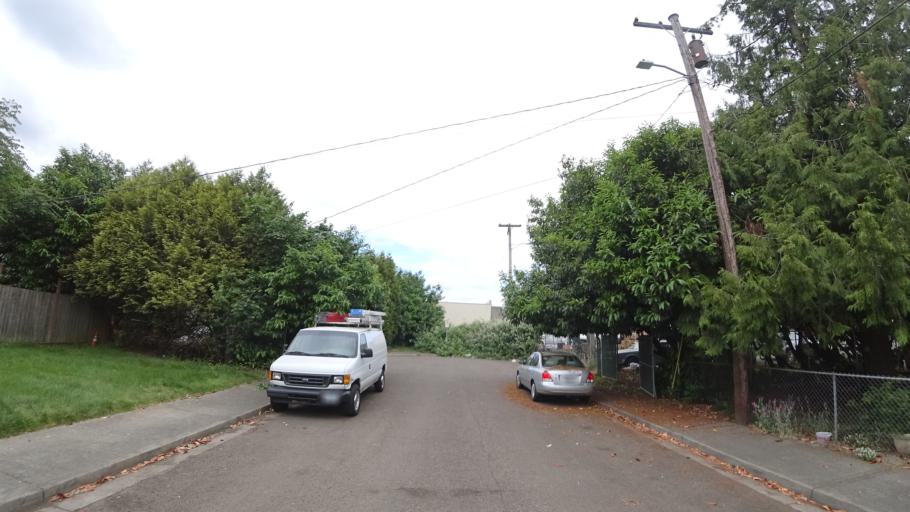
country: US
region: Oregon
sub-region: Multnomah County
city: Lents
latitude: 45.5030
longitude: -122.5358
